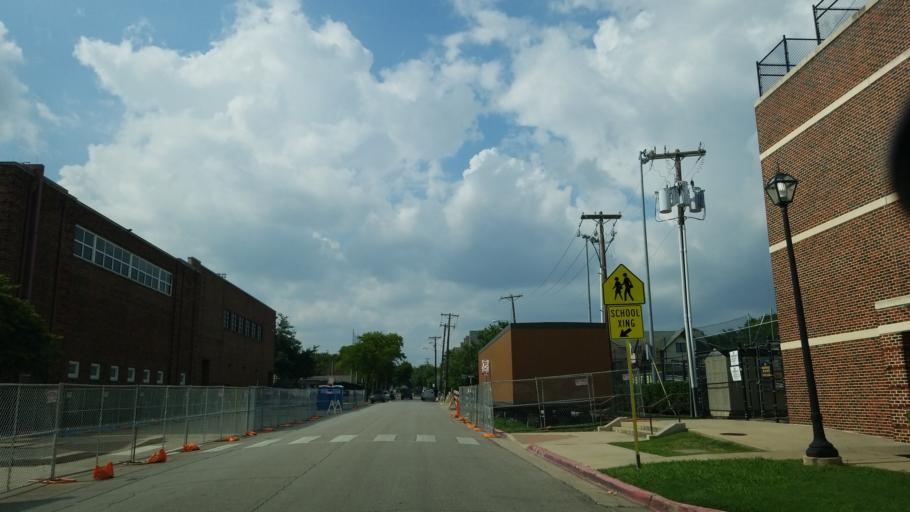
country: US
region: Texas
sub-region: Dallas County
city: University Park
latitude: 32.8474
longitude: -96.8068
